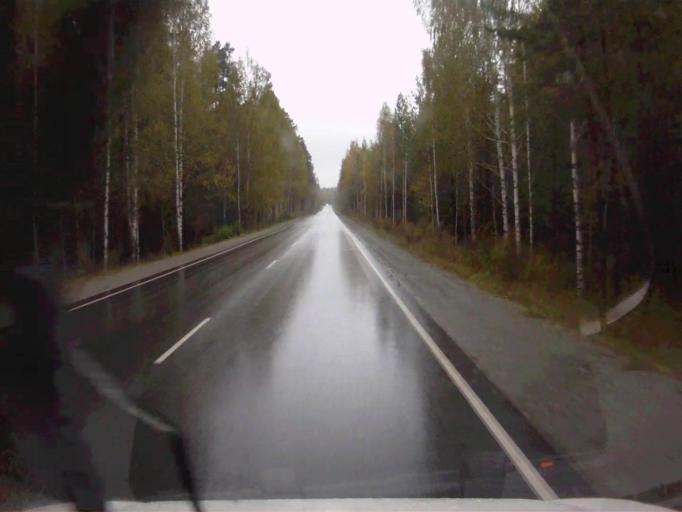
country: RU
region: Chelyabinsk
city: Kyshtym
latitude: 55.6480
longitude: 60.5831
